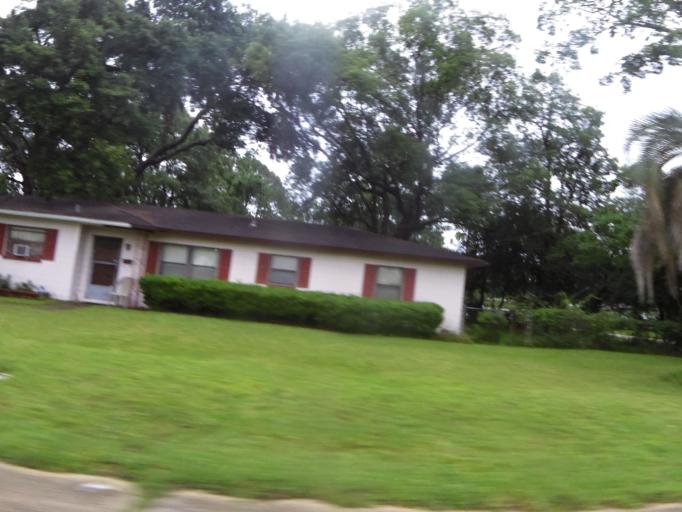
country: US
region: Florida
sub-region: Duval County
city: Jacksonville
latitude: 30.2884
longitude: -81.6309
